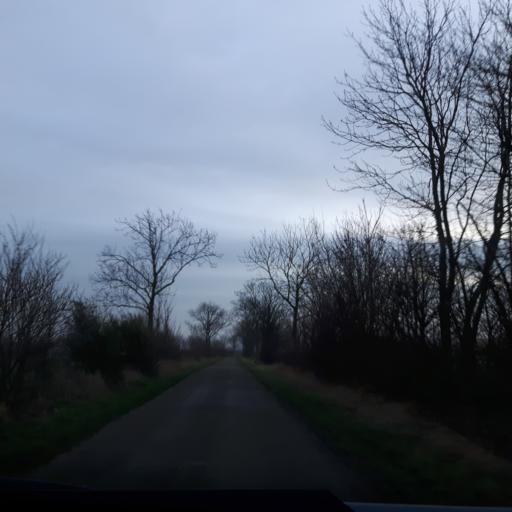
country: NL
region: Zeeland
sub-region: Gemeente Terneuzen
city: Terneuzen
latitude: 51.3990
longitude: 3.8457
